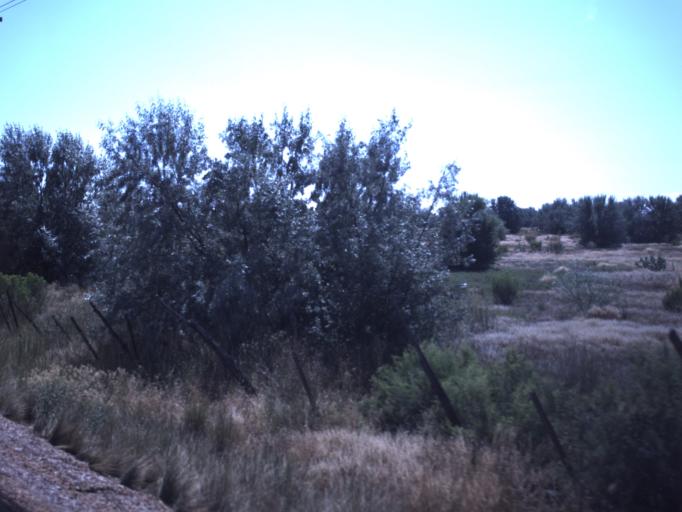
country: US
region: Utah
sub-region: Duchesne County
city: Roosevelt
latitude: 40.4037
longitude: -109.8436
